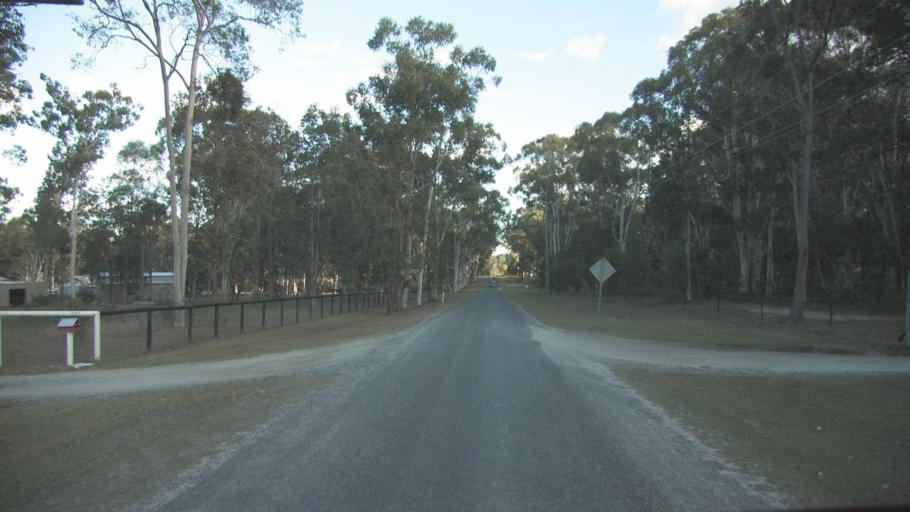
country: AU
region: Queensland
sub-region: Logan
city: Cedar Vale
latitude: -27.8451
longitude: 153.1107
